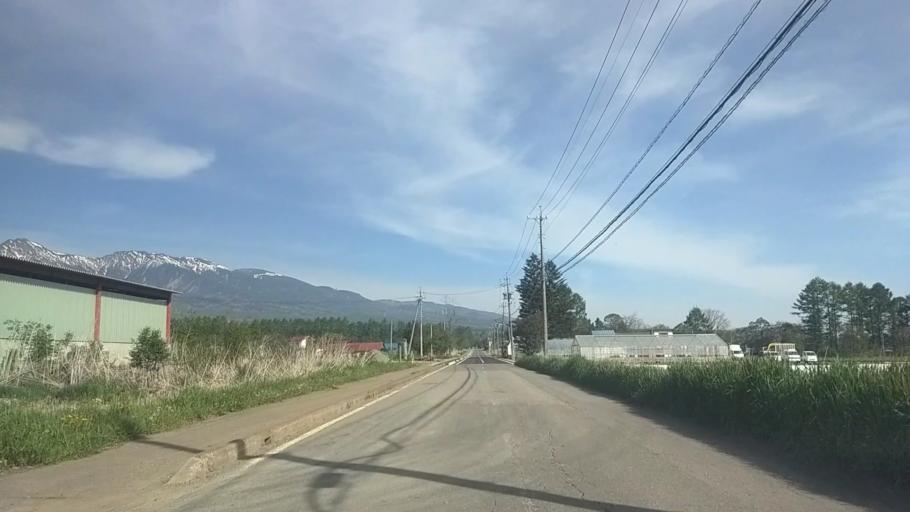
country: JP
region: Yamanashi
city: Nirasaki
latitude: 35.9458
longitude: 138.4788
